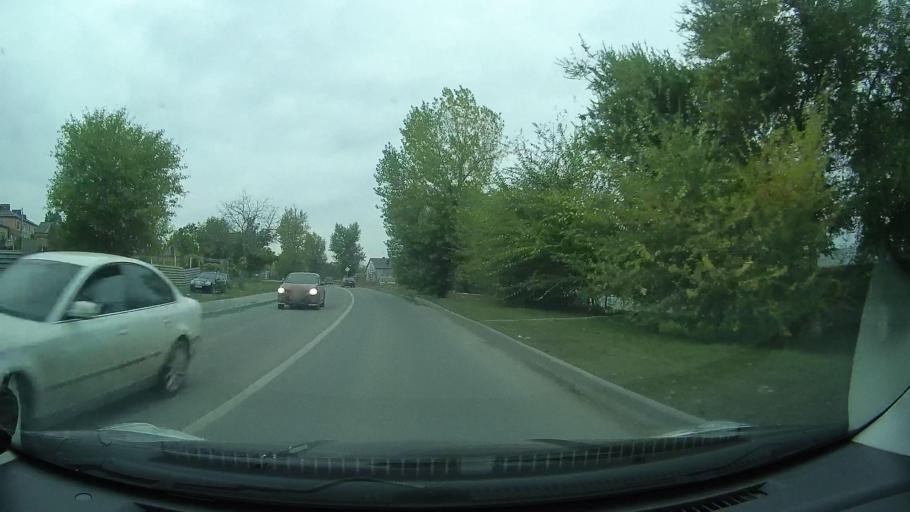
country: RU
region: Rostov
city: Severnyy
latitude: 47.2837
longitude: 39.6804
